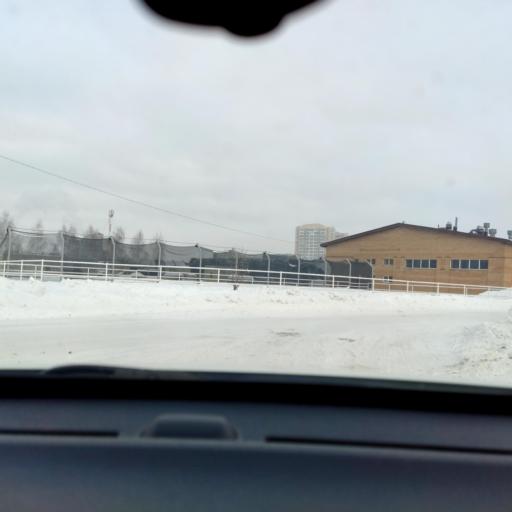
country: RU
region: Tatarstan
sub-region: Gorod Kazan'
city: Kazan
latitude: 55.7922
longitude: 49.2008
